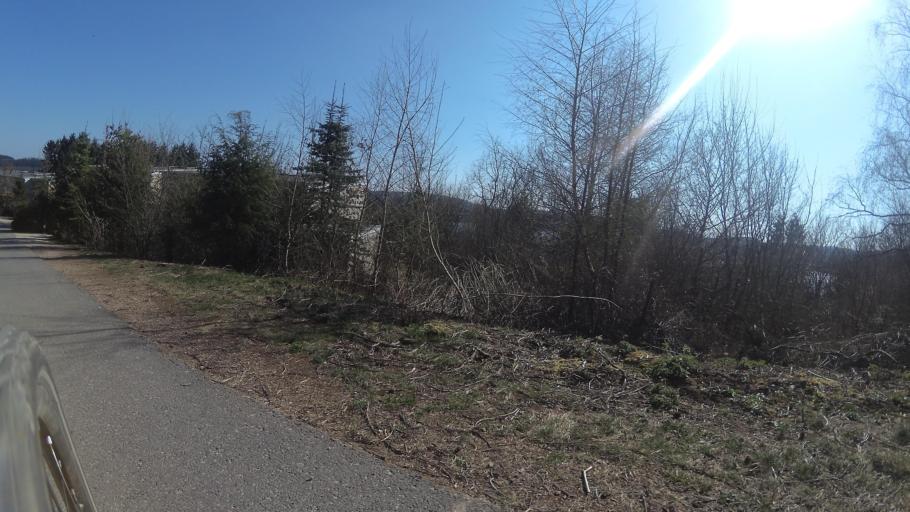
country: DE
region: Rheinland-Pfalz
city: Achtelsbach
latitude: 49.5737
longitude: 7.0787
